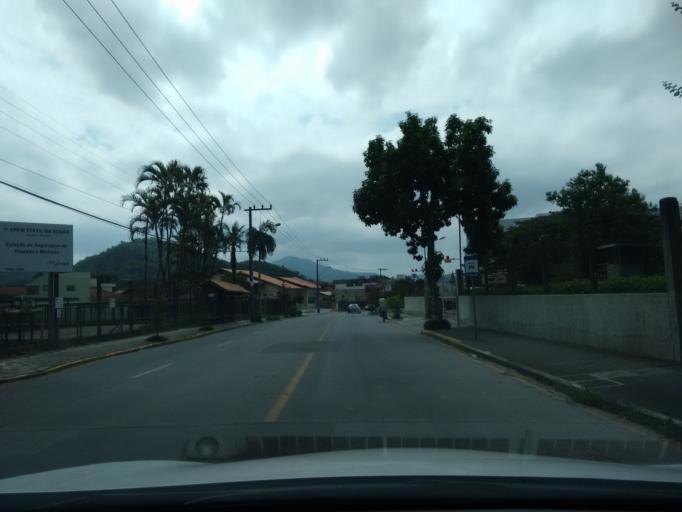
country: BR
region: Santa Catarina
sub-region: Jaragua Do Sul
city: Jaragua do Sul
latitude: -26.5133
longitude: -49.1272
